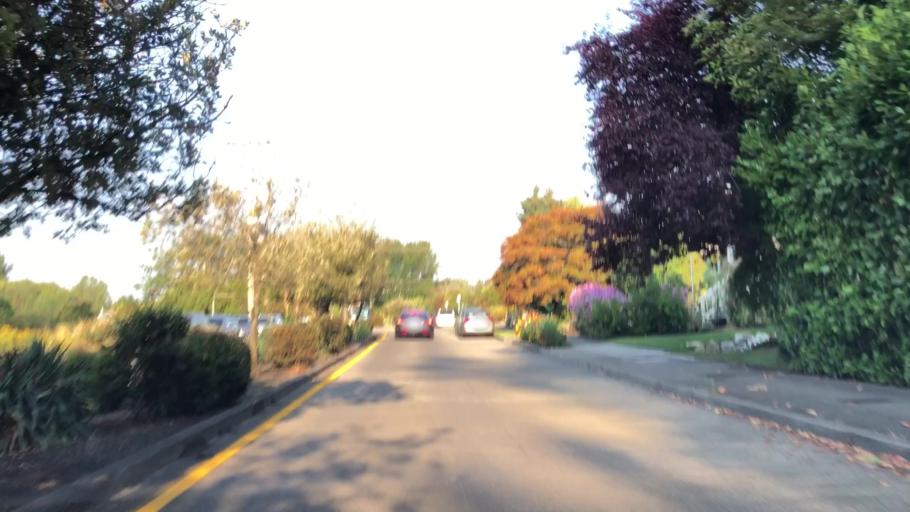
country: US
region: Washington
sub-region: King County
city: Seattle
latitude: 47.6585
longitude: -122.2873
